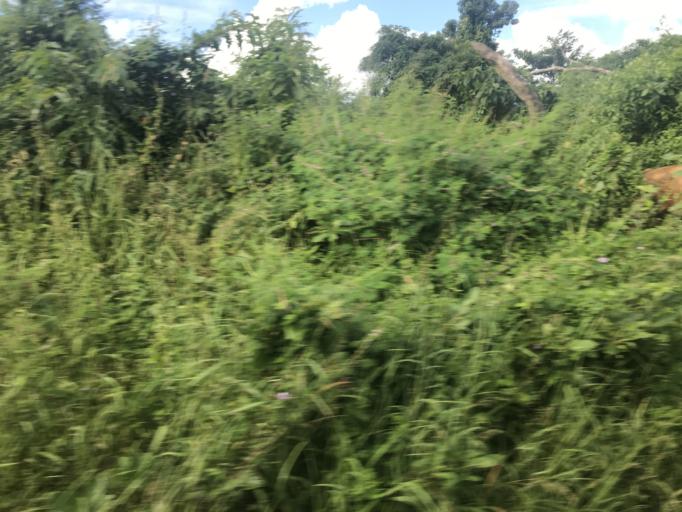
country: IN
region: Kerala
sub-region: Palakkad district
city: Palakkad
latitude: 10.8161
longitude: 76.6858
